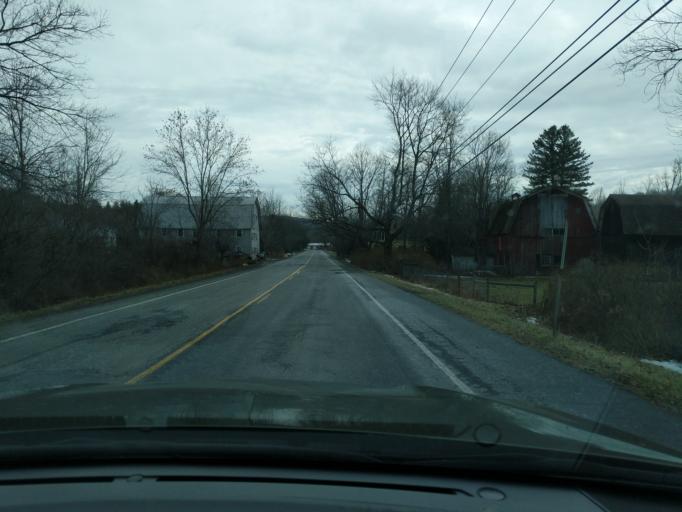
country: US
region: New York
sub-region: Tompkins County
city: East Ithaca
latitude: 42.3932
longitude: -76.4174
